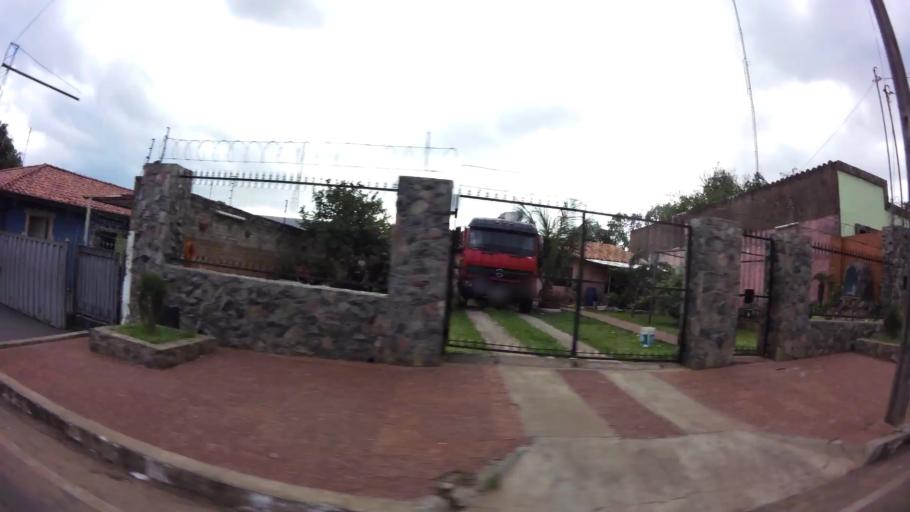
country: PY
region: Central
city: Fernando de la Mora
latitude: -25.3440
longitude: -57.5598
